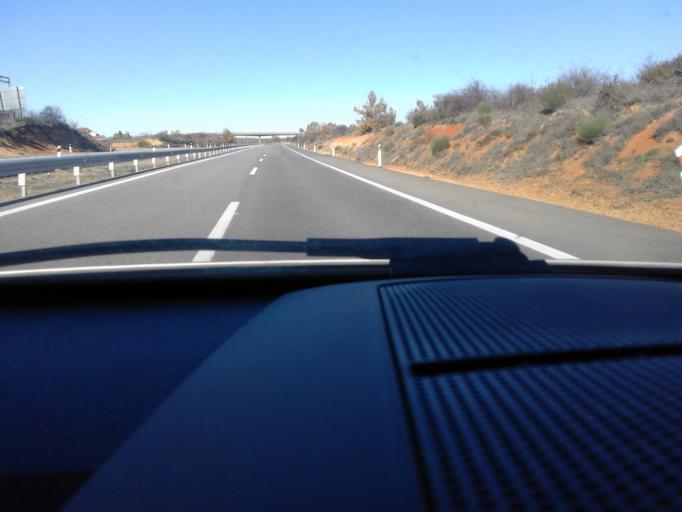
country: ES
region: Castille and Leon
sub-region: Provincia de Leon
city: Valverde de la Virgen
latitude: 42.5874
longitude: -5.6812
